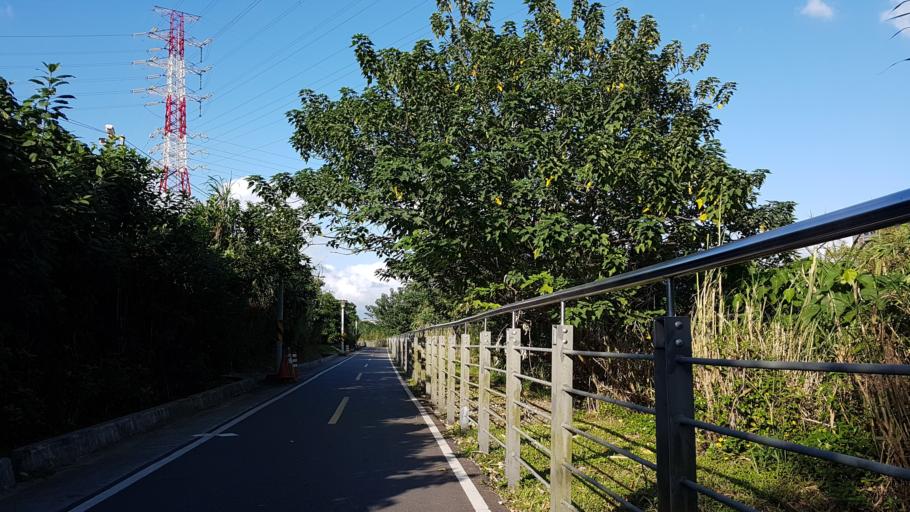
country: TW
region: Taipei
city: Taipei
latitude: 25.0008
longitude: 121.5308
